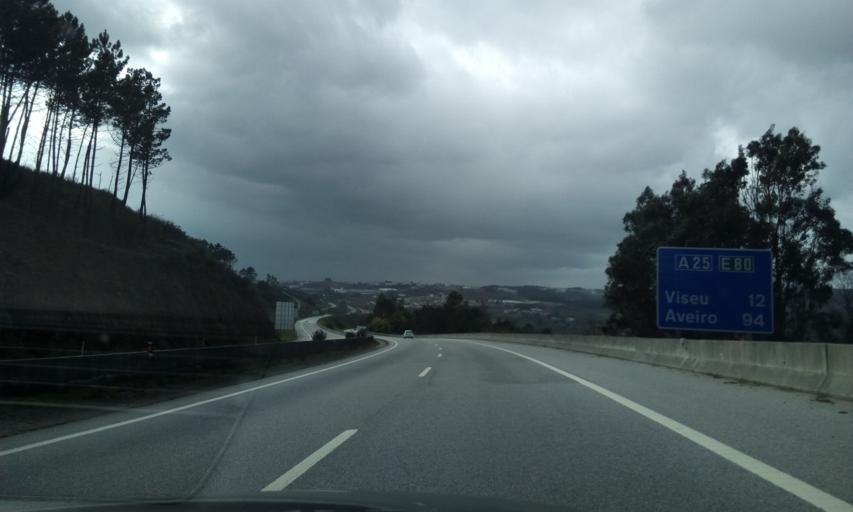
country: PT
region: Viseu
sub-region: Mangualde
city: Mangualde
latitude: 40.6331
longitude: -7.8081
